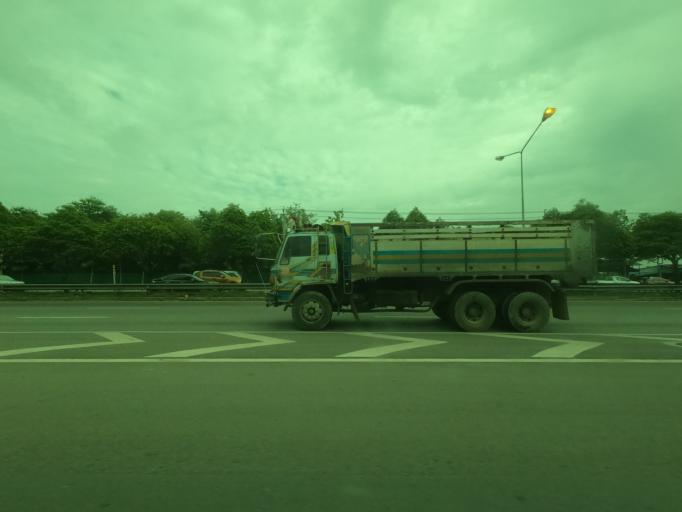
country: TH
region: Bangkok
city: Thawi Watthana
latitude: 13.7879
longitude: 100.3466
